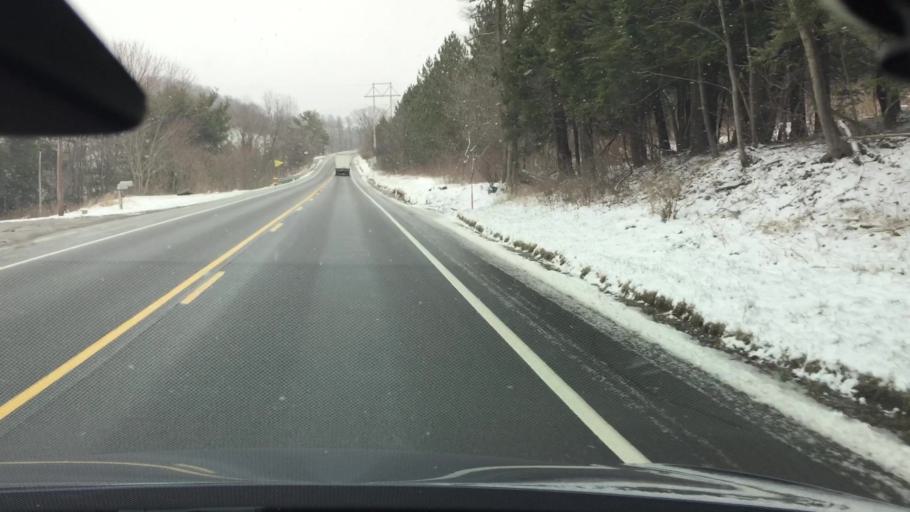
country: US
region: Pennsylvania
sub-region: Jefferson County
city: Brookville
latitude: 41.0493
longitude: -79.2528
